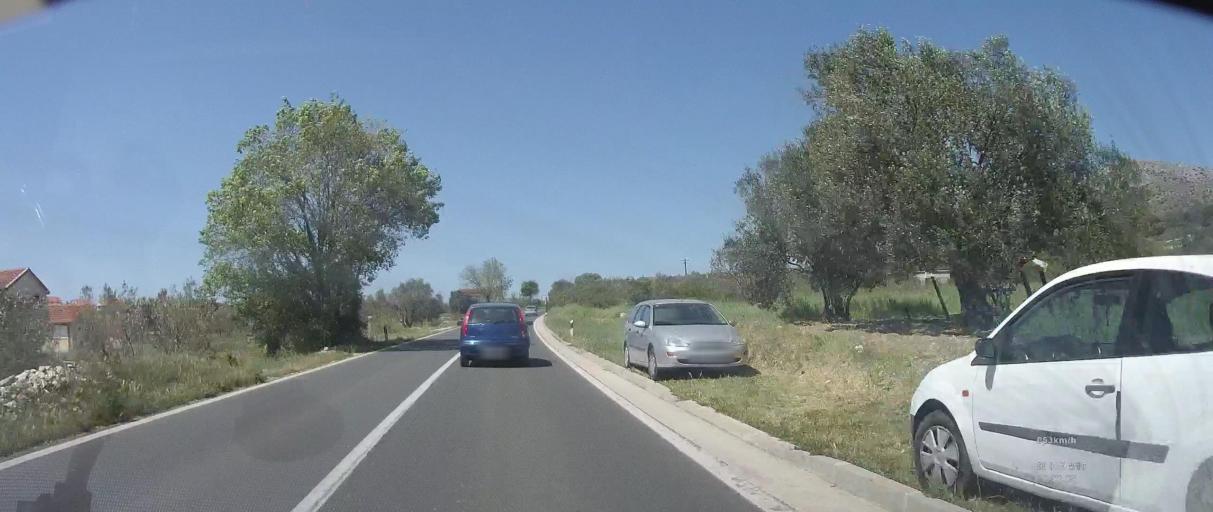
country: HR
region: Sibensko-Kniniska
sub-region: Grad Sibenik
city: Brodarica
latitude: 43.7030
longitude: 15.9360
